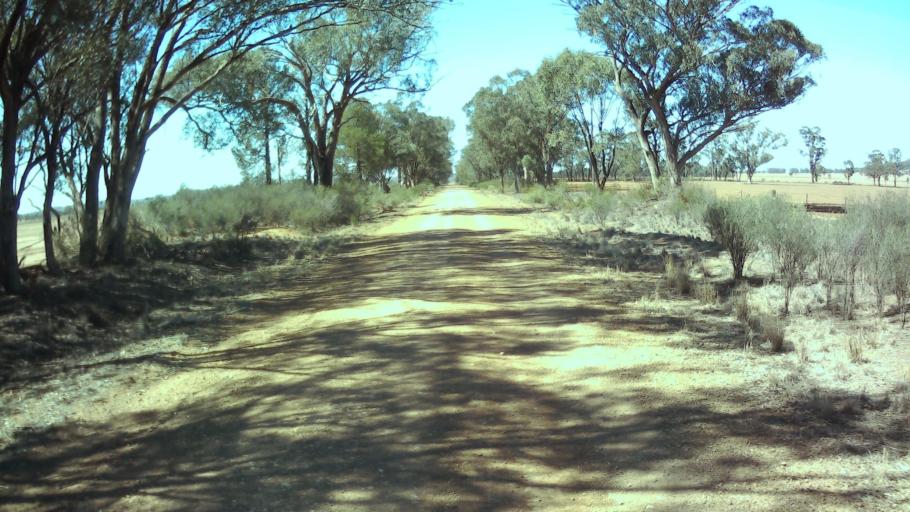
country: AU
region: New South Wales
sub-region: Weddin
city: Grenfell
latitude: -33.7092
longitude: 147.9708
